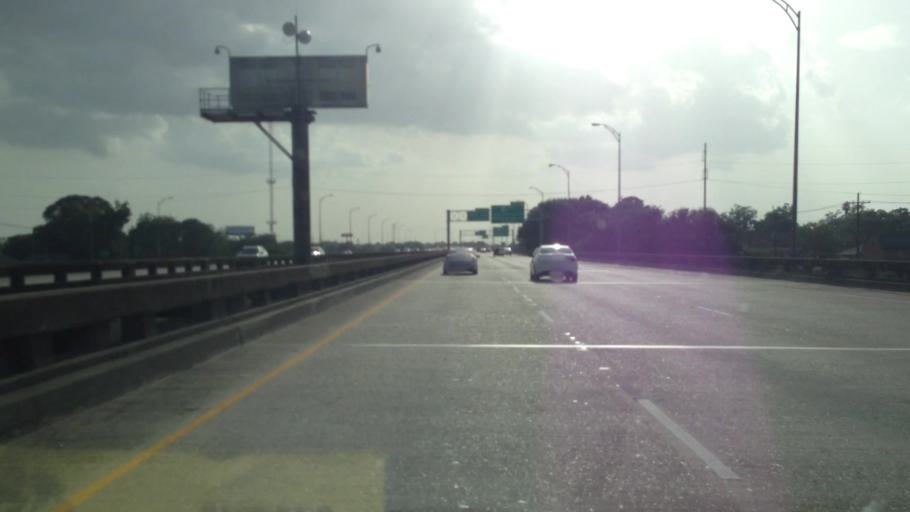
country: US
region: Louisiana
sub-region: Orleans Parish
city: New Orleans
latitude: 29.9912
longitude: -90.0631
